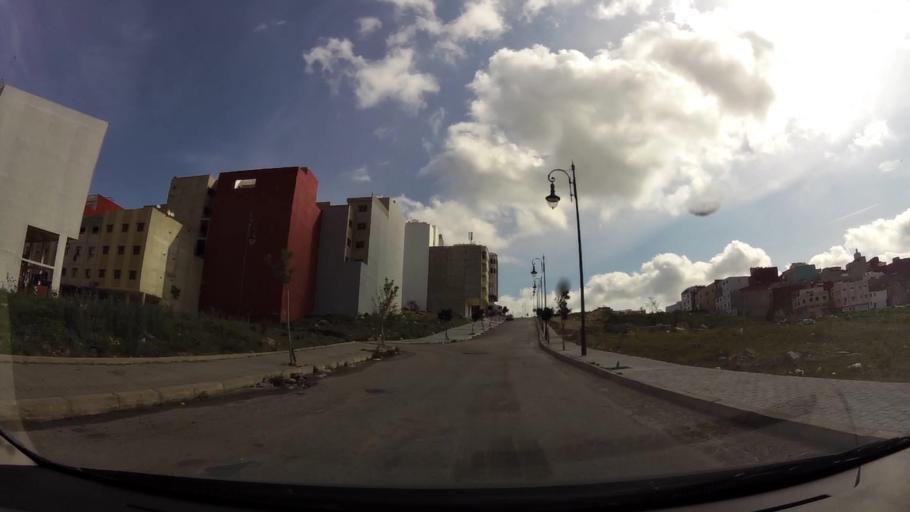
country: MA
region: Tanger-Tetouan
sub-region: Tanger-Assilah
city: Tangier
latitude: 35.7654
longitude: -5.7670
